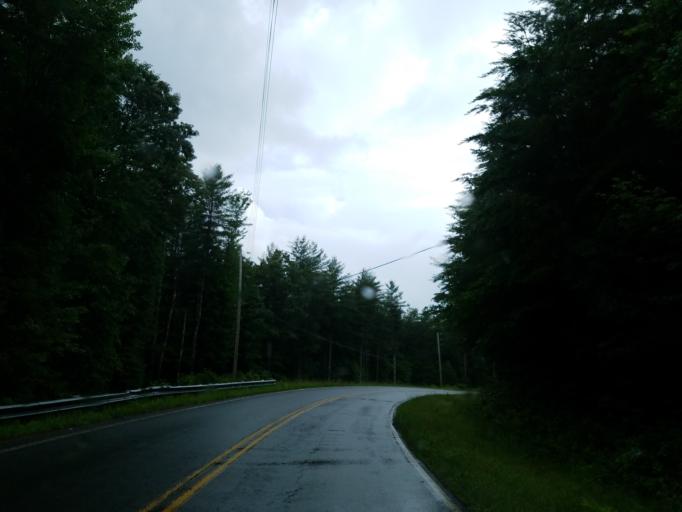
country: US
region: Georgia
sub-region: Fannin County
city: Blue Ridge
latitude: 34.7689
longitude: -84.2567
